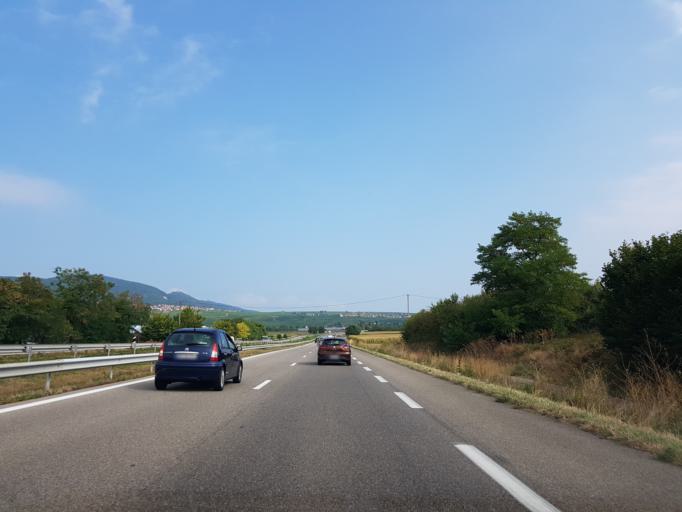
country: FR
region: Alsace
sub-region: Departement du Haut-Rhin
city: Pfaffenheim
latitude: 47.9906
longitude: 7.2940
